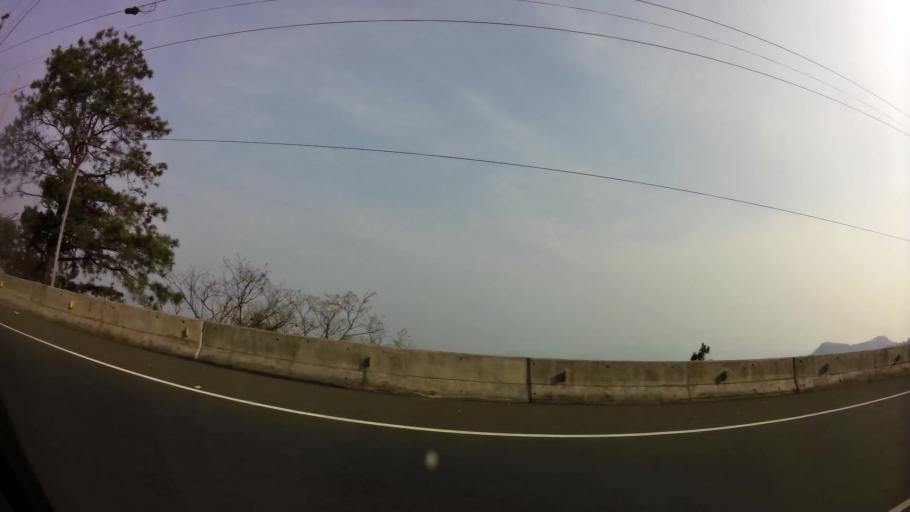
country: HN
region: Comayagua
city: Flores
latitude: 14.2912
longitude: -87.4913
